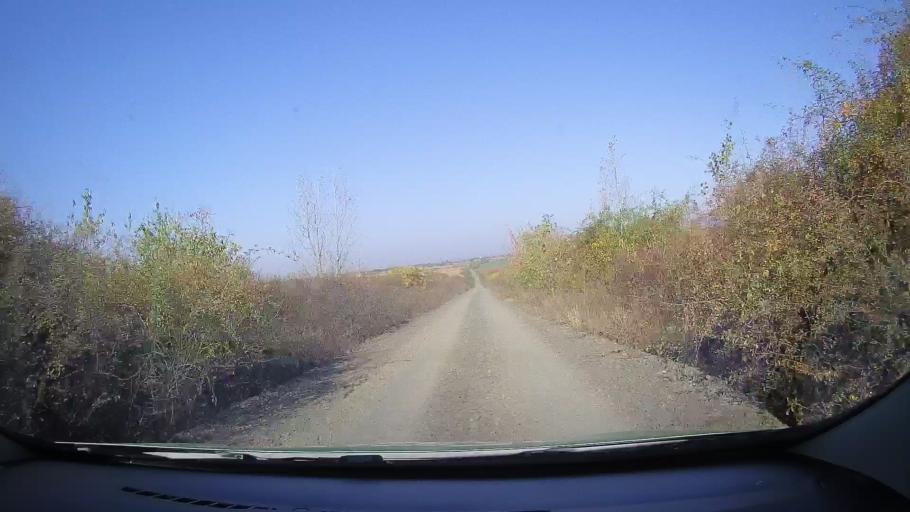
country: RO
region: Satu Mare
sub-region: Comuna Sauca
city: Sauca
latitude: 47.4787
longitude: 22.4728
